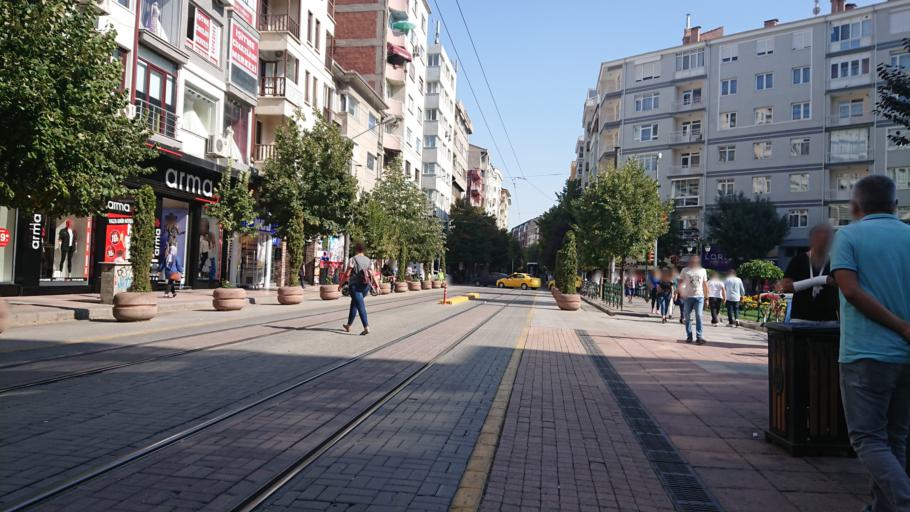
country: TR
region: Eskisehir
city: Eskisehir
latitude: 39.7790
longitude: 30.5142
